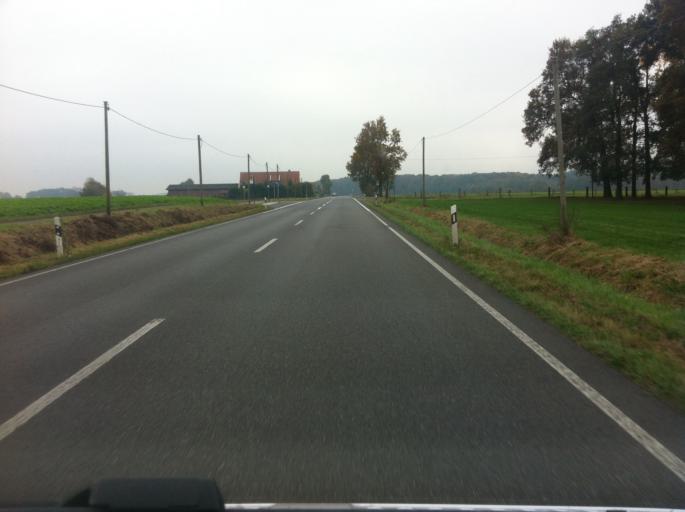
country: DE
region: North Rhine-Westphalia
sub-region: Regierungsbezirk Munster
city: Sudlohn
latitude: 51.9489
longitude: 6.8195
